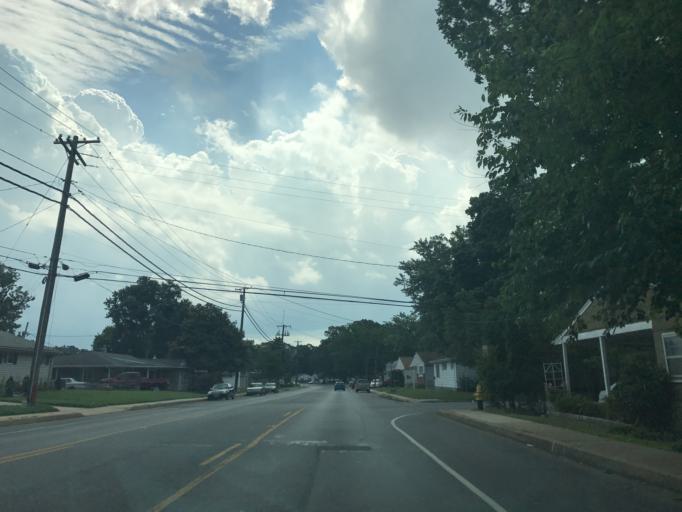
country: US
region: Maryland
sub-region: Anne Arundel County
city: Glen Burnie
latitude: 39.1521
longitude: -76.6294
